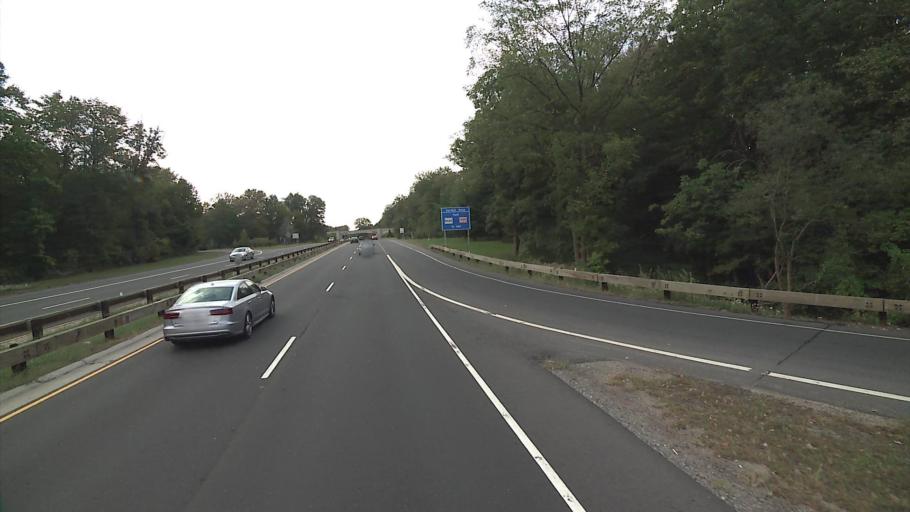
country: US
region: Connecticut
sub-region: Fairfield County
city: New Canaan
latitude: 41.1181
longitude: -73.4860
